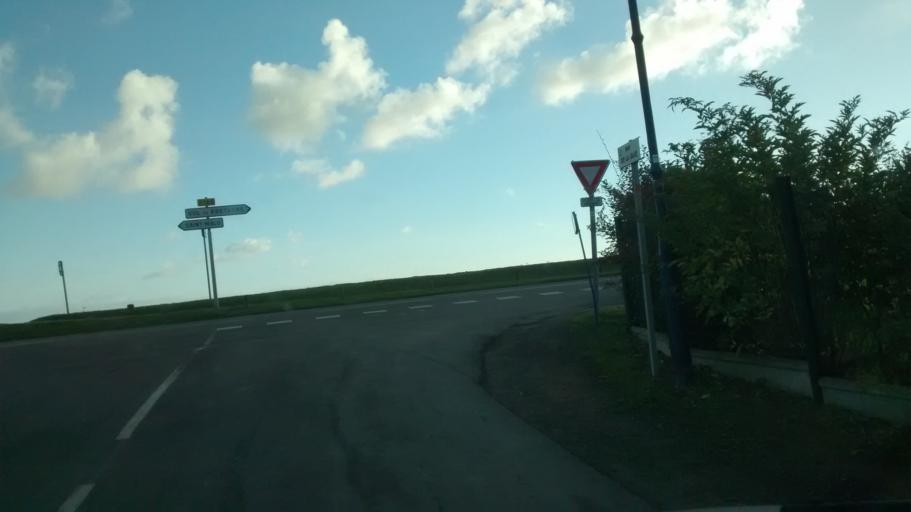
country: FR
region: Brittany
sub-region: Departement d'Ille-et-Vilaine
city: La Fresnais
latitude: 48.6244
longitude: -1.8578
